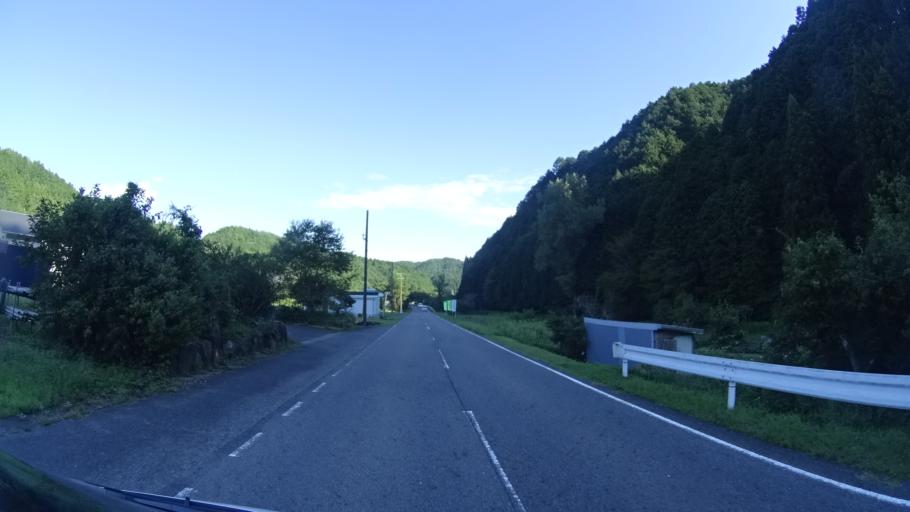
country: JP
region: Gifu
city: Minokamo
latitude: 35.5825
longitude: 137.0849
